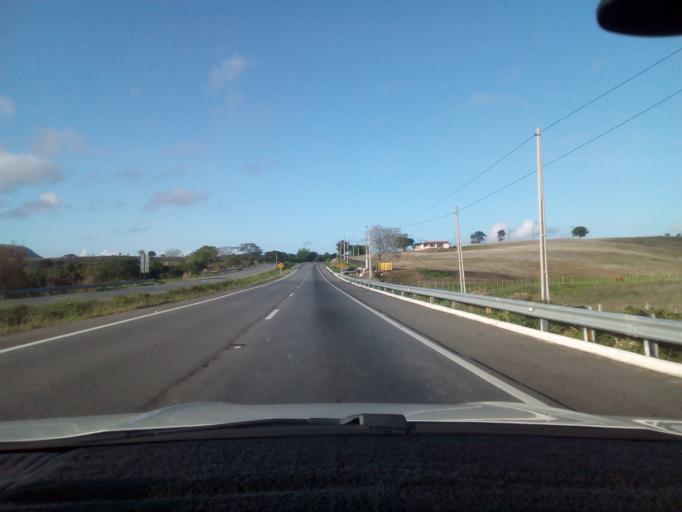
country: BR
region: Paraiba
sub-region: Inga
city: Inga
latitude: -7.2307
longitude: -35.6002
